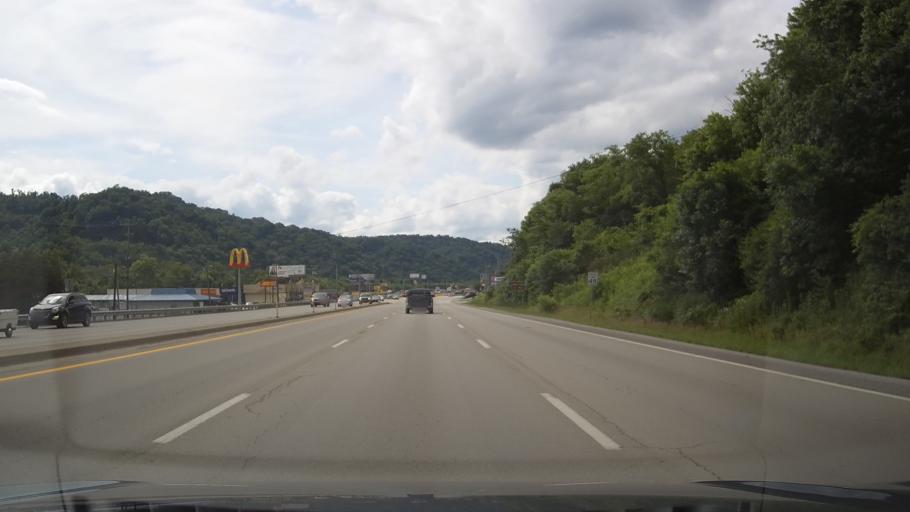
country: US
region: Kentucky
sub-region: Pike County
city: Coal Run Village
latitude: 37.5176
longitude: -82.5634
